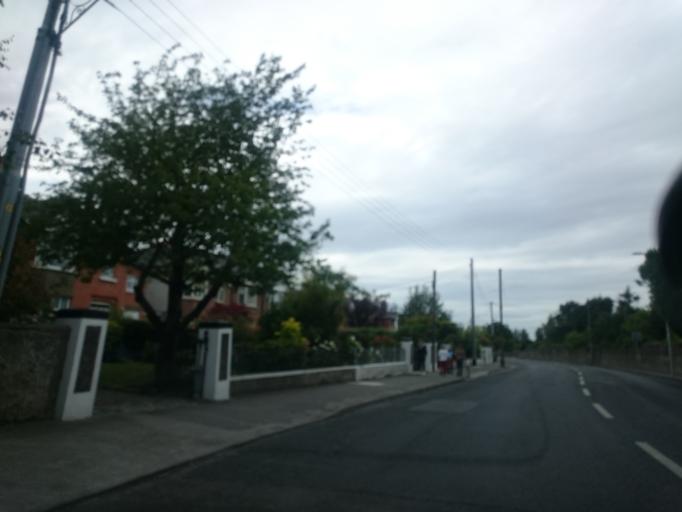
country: IE
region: Leinster
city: Templeogue
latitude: 53.3042
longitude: -6.2996
